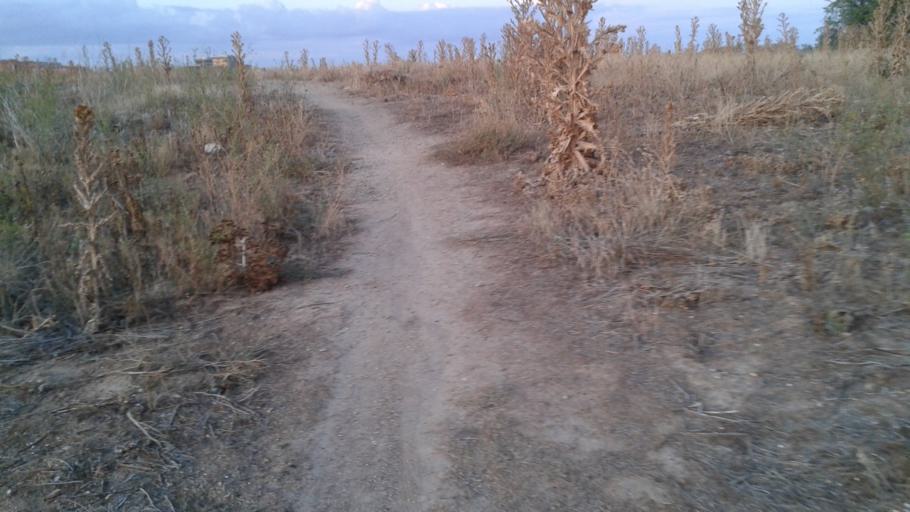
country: ES
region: Castille and Leon
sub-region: Provincia de Valladolid
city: Arroyo
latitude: 41.6063
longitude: -4.8049
